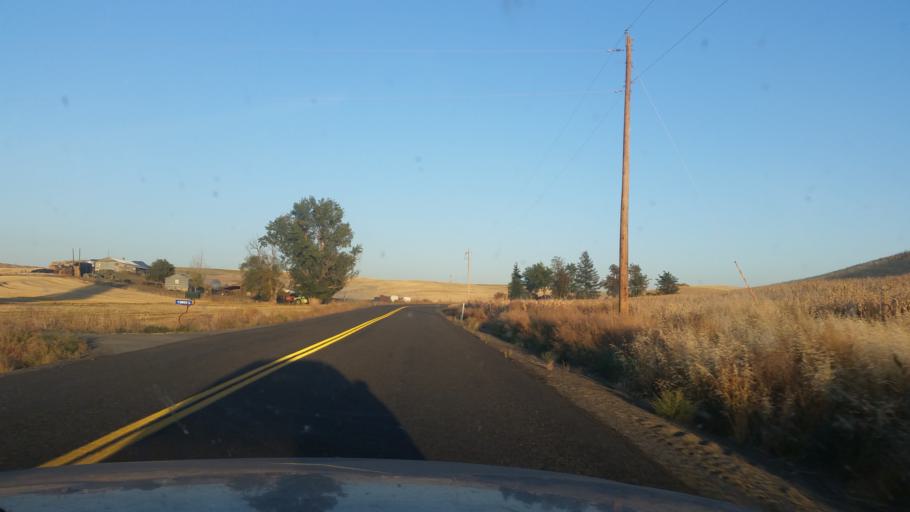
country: US
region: Washington
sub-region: Spokane County
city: Medical Lake
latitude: 47.5364
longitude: -117.6267
